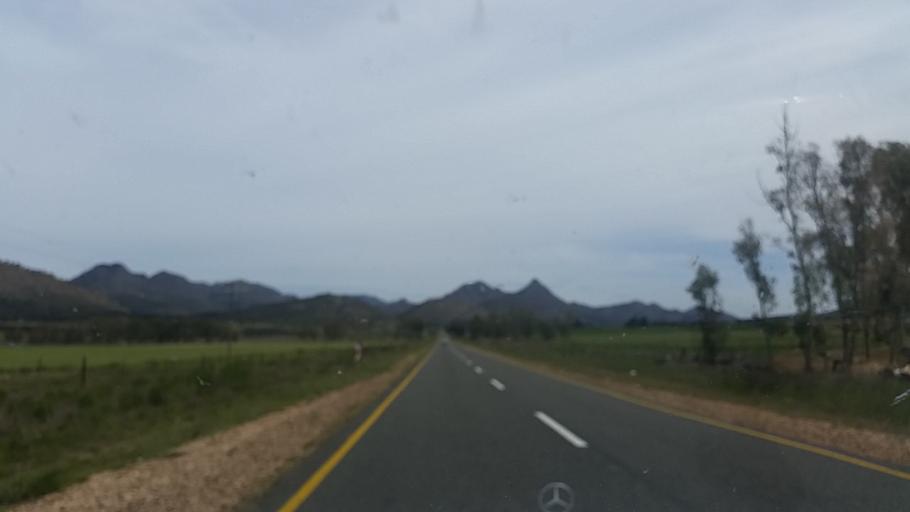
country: ZA
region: Western Cape
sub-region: Eden District Municipality
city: George
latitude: -33.8245
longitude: 22.4811
